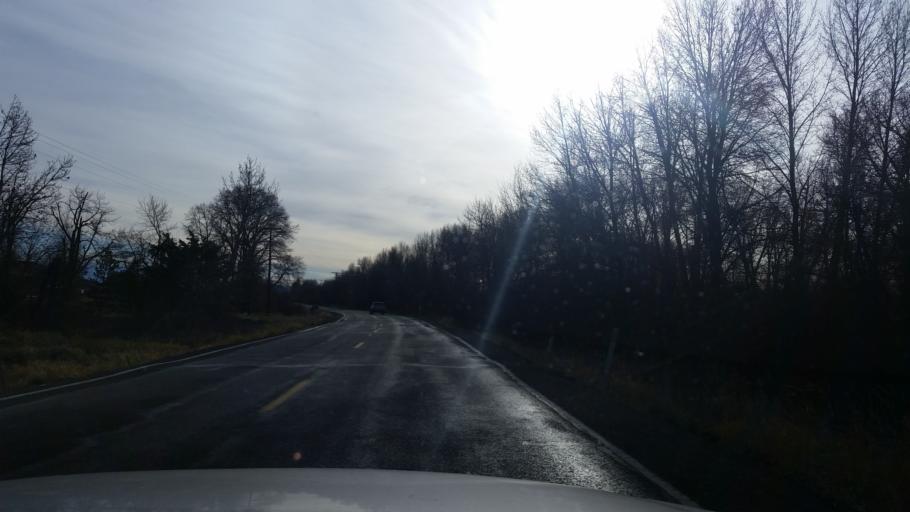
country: US
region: Washington
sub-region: Kittitas County
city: Ellensburg
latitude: 47.0581
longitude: -120.6448
